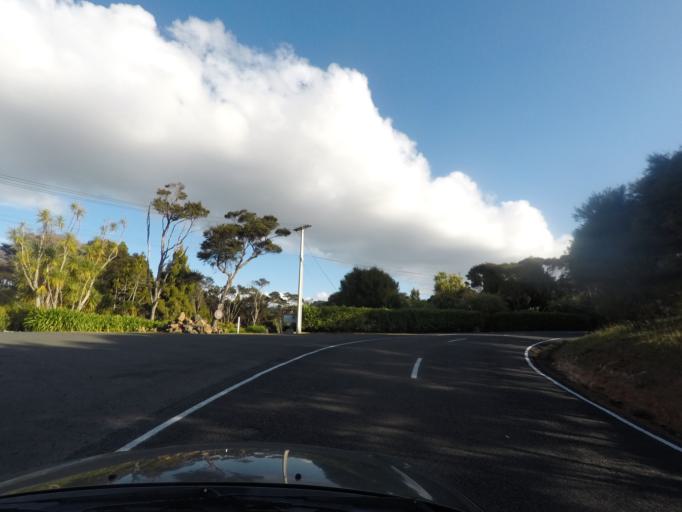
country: NZ
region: Auckland
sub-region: Auckland
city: Titirangi
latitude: -36.9277
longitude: 174.6209
